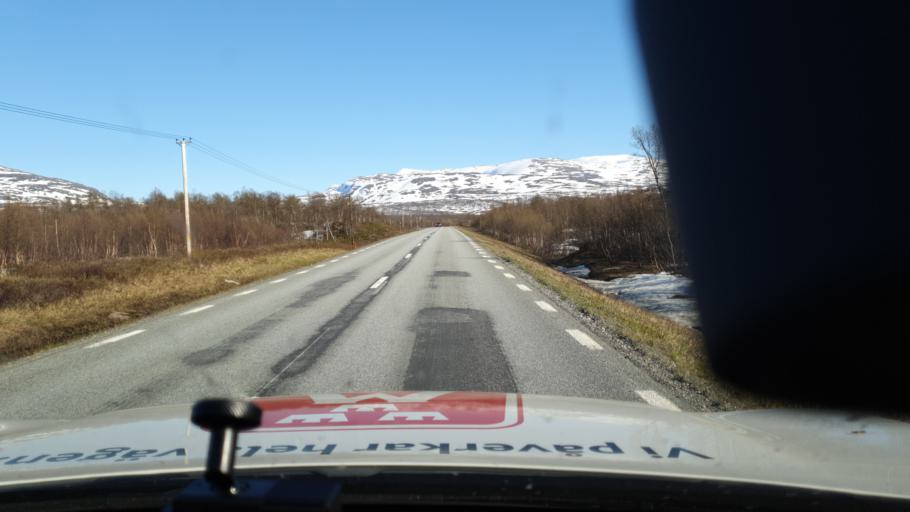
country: NO
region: Nordland
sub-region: Rana
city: Mo i Rana
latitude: 66.0324
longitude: 15.0728
